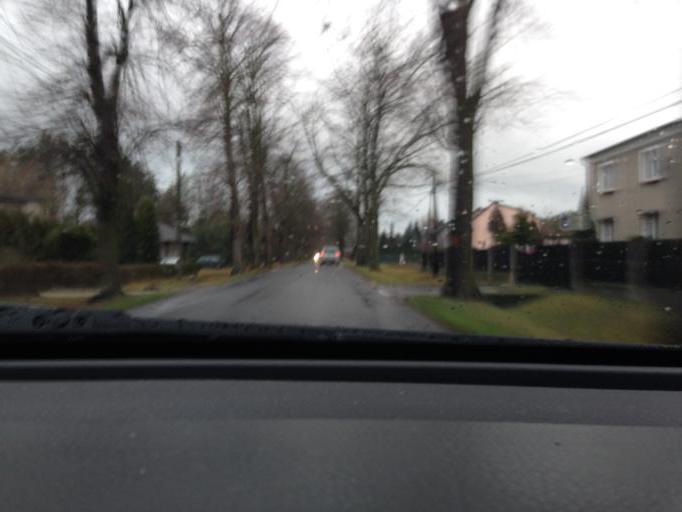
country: PL
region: Opole Voivodeship
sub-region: Powiat opolski
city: Wegry
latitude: 50.7265
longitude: 18.0308
